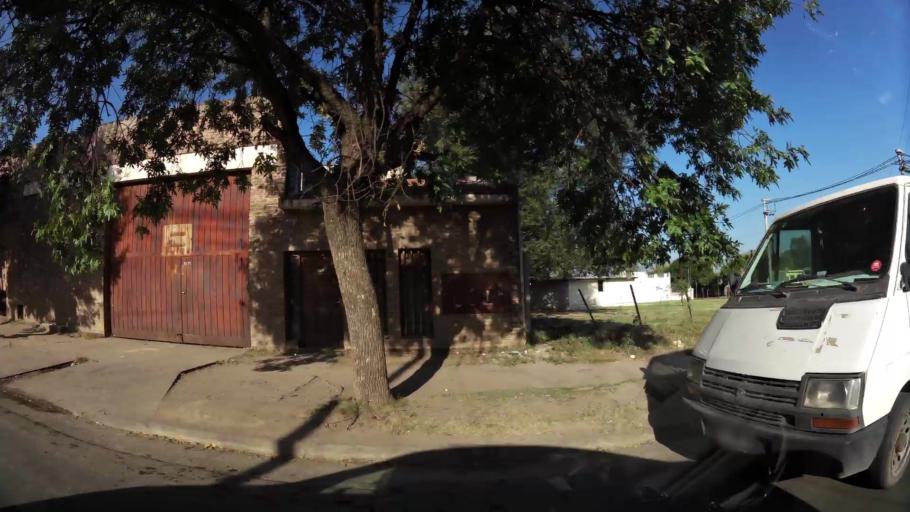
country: AR
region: Cordoba
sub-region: Departamento de Capital
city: Cordoba
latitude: -31.4470
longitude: -64.2481
